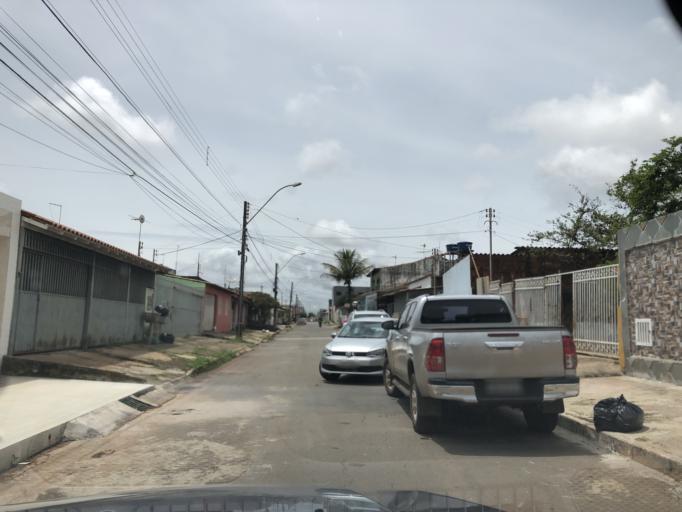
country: BR
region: Federal District
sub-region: Brasilia
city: Brasilia
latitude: -15.8082
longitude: -48.1043
